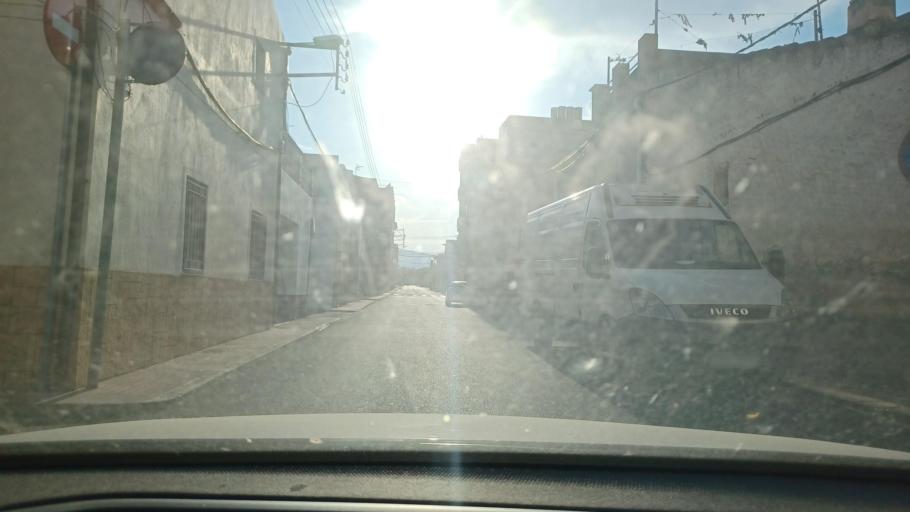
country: ES
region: Catalonia
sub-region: Provincia de Tarragona
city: Santa Barbara
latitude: 40.7128
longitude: 0.4939
